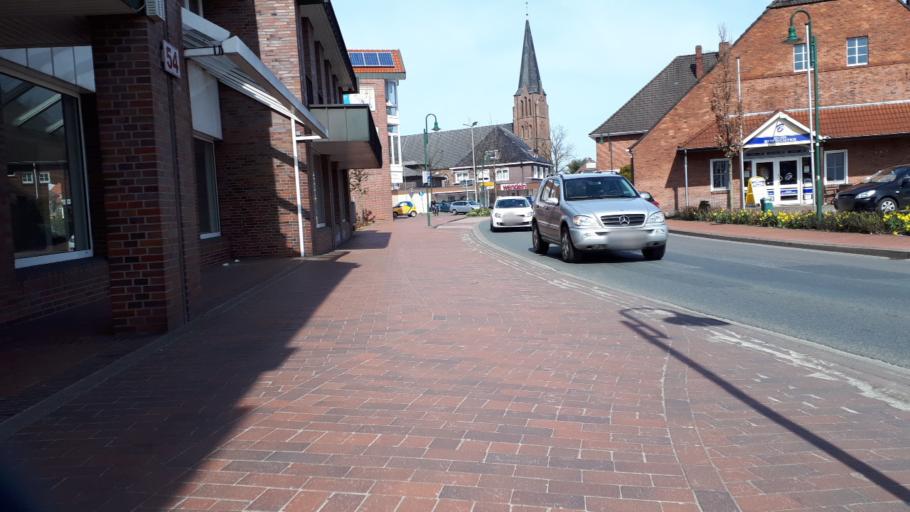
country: DE
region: Lower Saxony
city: Garrel
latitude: 52.9542
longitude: 8.0243
